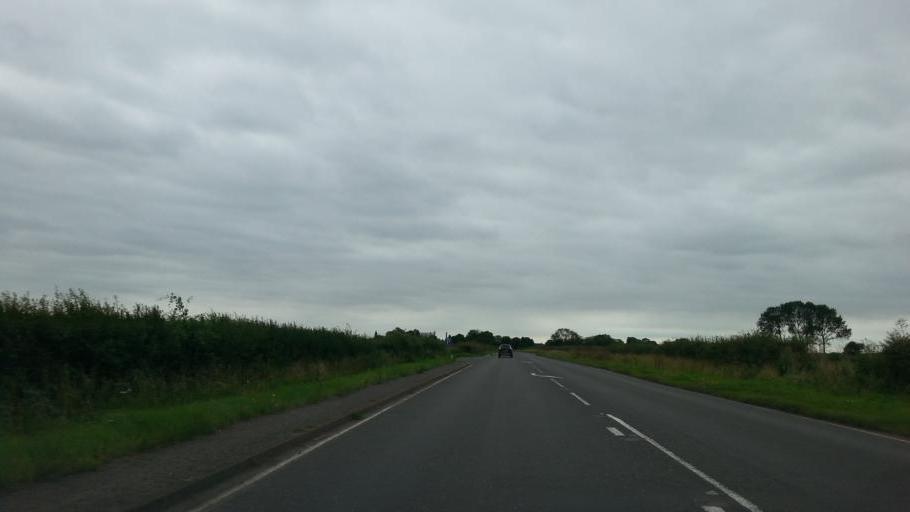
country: GB
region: England
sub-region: Nottinghamshire
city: Newark on Trent
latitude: 53.1147
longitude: -0.8205
